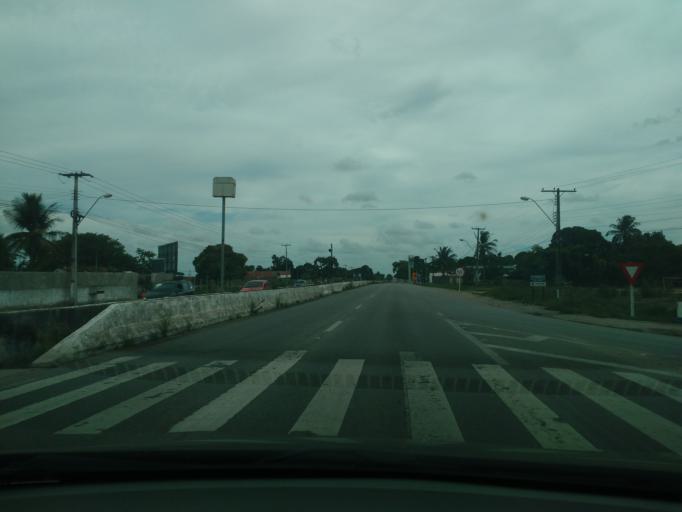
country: BR
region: Alagoas
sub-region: Rio Largo
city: Rio Largo
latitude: -9.4745
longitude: -35.8220
